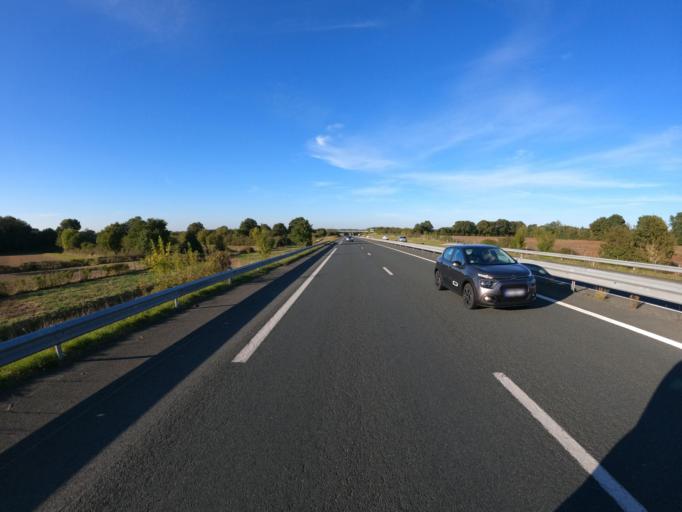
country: FR
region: Pays de la Loire
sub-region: Departement de Maine-et-Loire
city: Mazieres-en-Mauges
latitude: 47.0711
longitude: -0.8264
